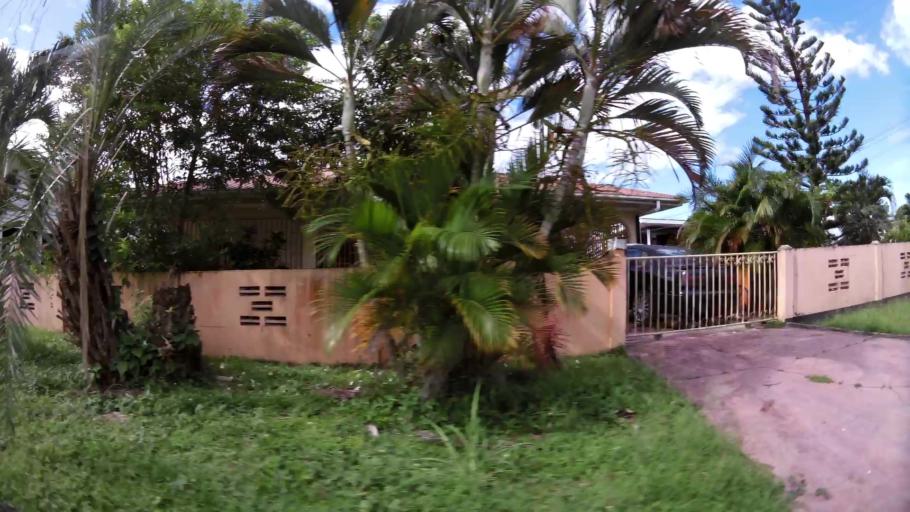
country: SR
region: Paramaribo
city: Paramaribo
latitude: 5.8477
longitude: -55.1514
